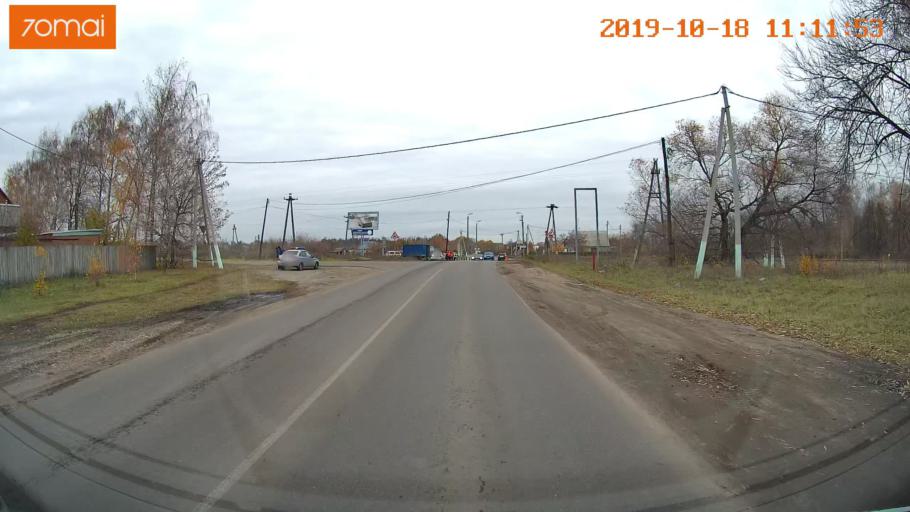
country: RU
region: Tula
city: Kimovsk
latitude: 53.9623
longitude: 38.5517
